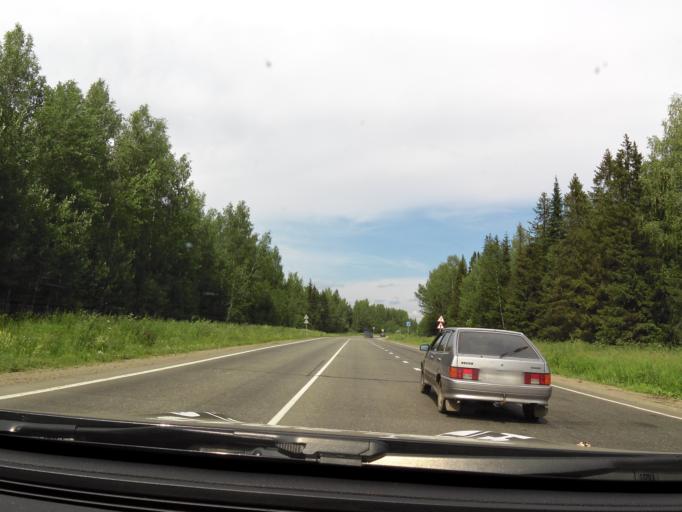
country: RU
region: Kirov
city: Vakhrushi
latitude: 58.6631
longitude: 49.9263
